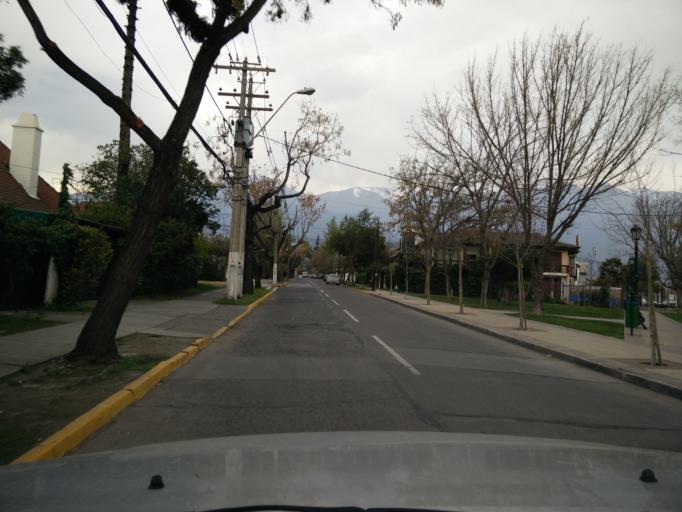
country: CL
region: Santiago Metropolitan
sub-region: Provincia de Santiago
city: Villa Presidente Frei, Nunoa, Santiago, Chile
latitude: -33.4143
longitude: -70.5575
